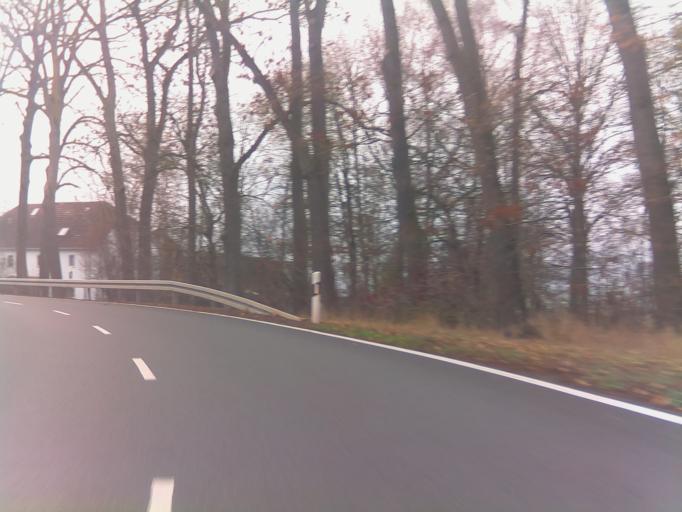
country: DE
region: Thuringia
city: Romhild
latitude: 50.4179
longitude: 10.5322
